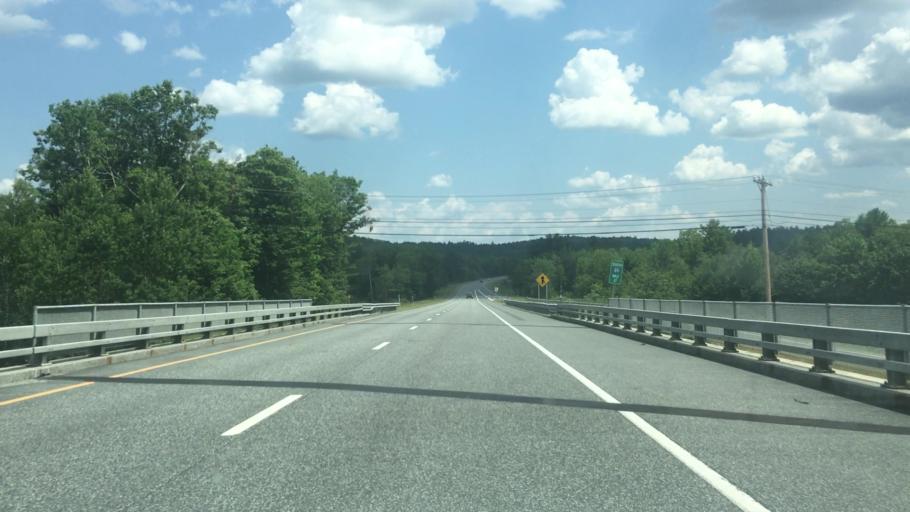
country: US
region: New Hampshire
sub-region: Sullivan County
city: Sunapee
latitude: 43.4414
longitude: -72.0645
